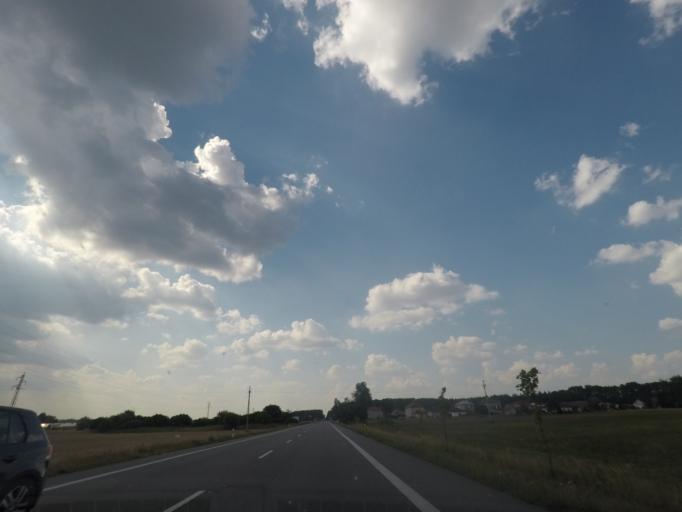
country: CZ
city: Albrechtice nad Orlici
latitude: 50.1697
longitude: 16.0416
